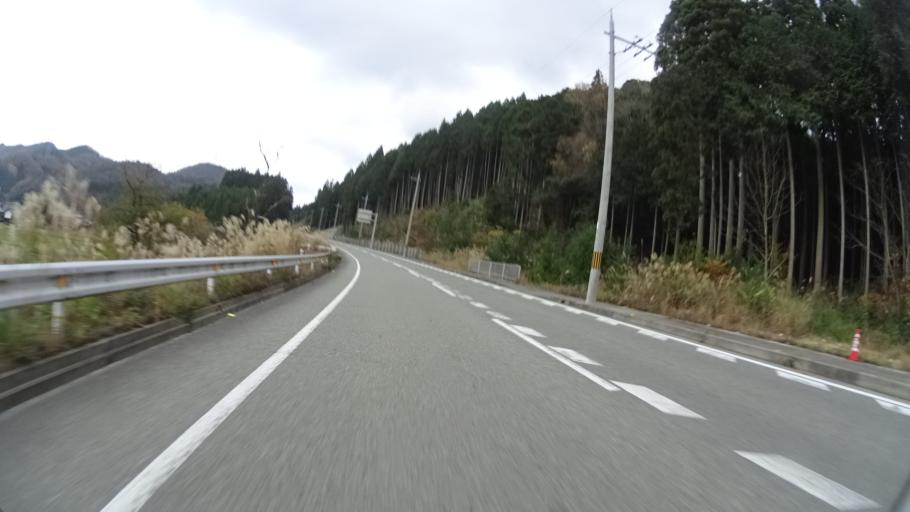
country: JP
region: Hyogo
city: Sasayama
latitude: 35.0660
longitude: 135.4036
